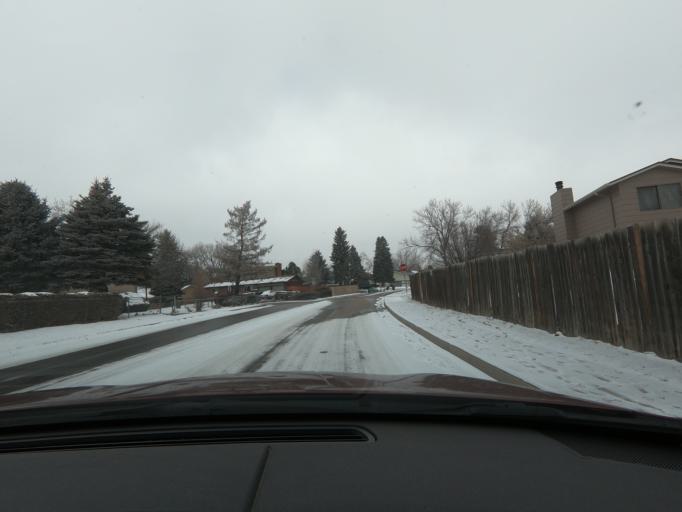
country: US
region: Colorado
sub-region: El Paso County
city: Security-Widefield
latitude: 38.7261
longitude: -104.6934
